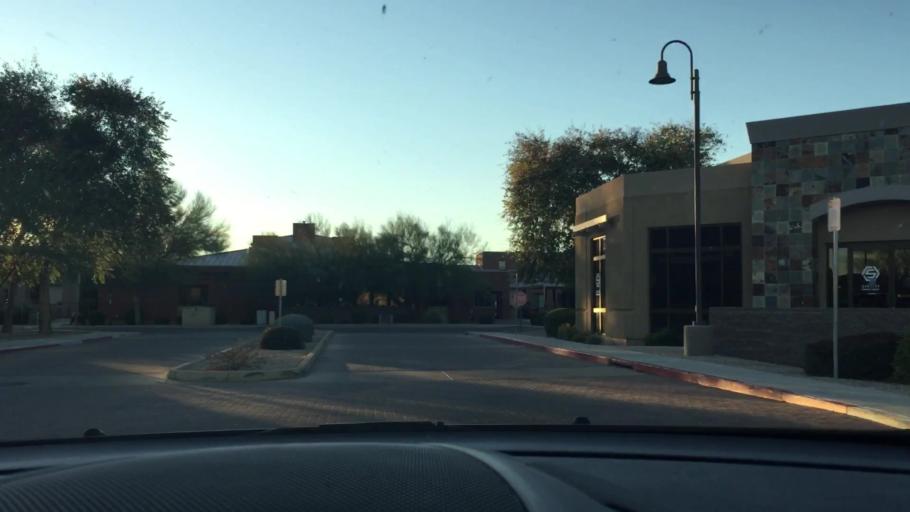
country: US
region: Arizona
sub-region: Maricopa County
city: Scottsdale
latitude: 33.5766
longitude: -111.8756
